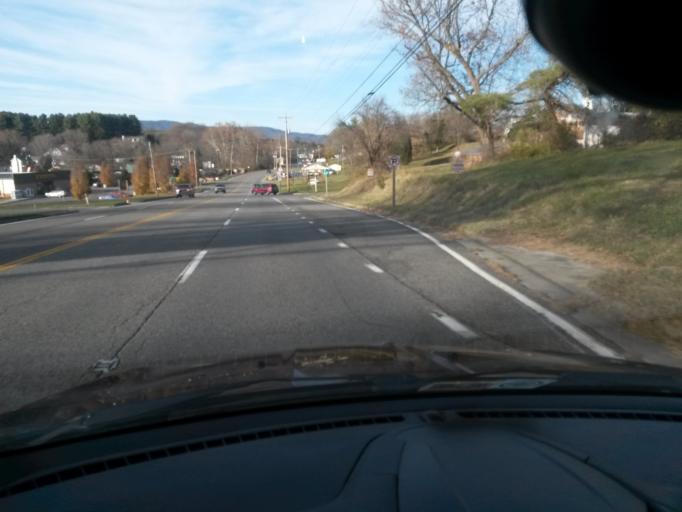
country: US
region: Virginia
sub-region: Botetourt County
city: Fincastle
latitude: 37.4953
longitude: -79.8787
